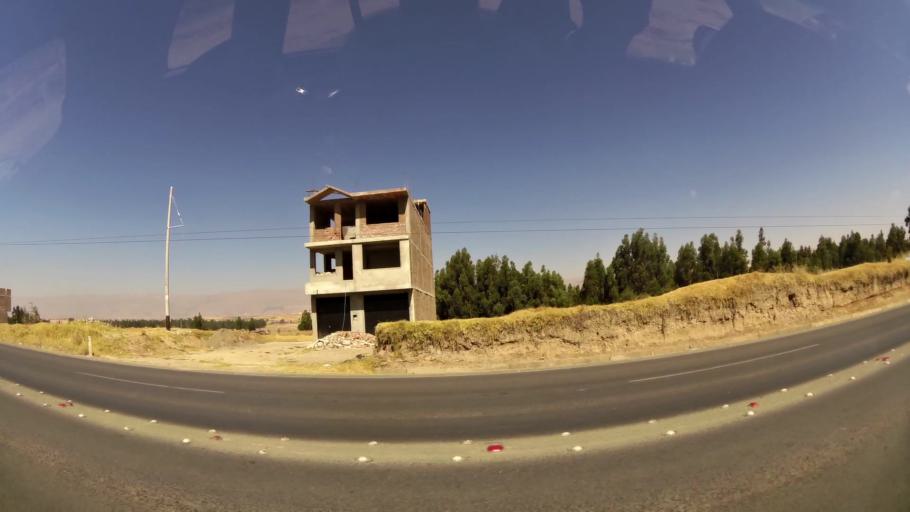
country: PE
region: Junin
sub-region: Provincia de Huancayo
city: San Agustin
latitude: -11.9735
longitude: -75.2673
